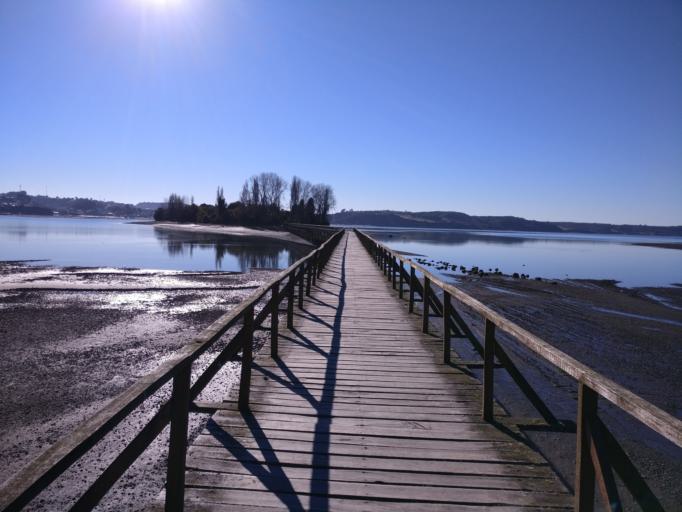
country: CL
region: Los Lagos
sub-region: Provincia de Chiloe
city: Castro
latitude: -42.1649
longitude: -73.4816
